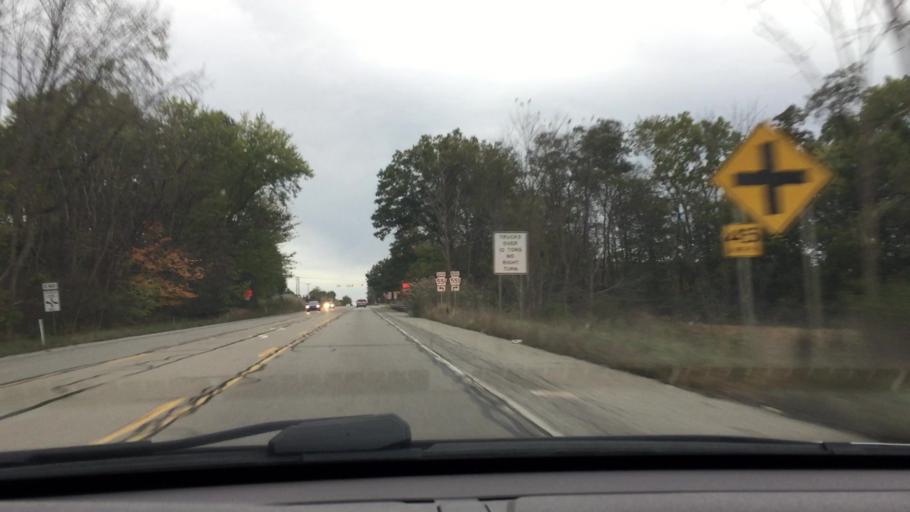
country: US
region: Pennsylvania
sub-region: Lawrence County
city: Oakwood
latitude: 41.0516
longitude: -80.4370
